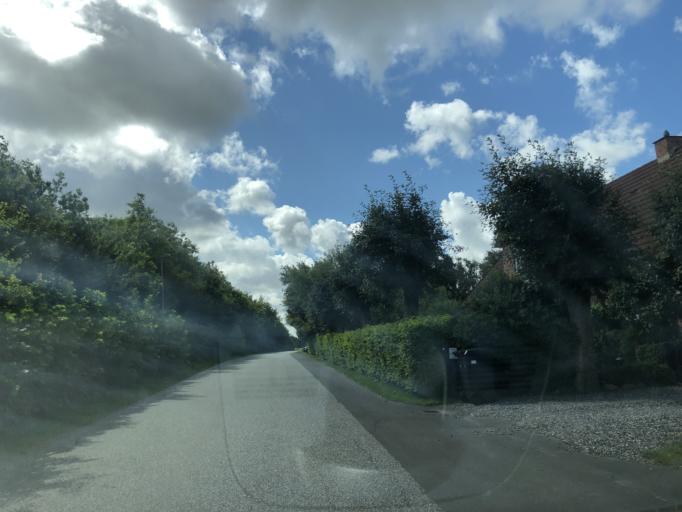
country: DK
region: Central Jutland
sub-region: Struer Kommune
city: Struer
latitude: 56.4636
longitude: 8.5226
